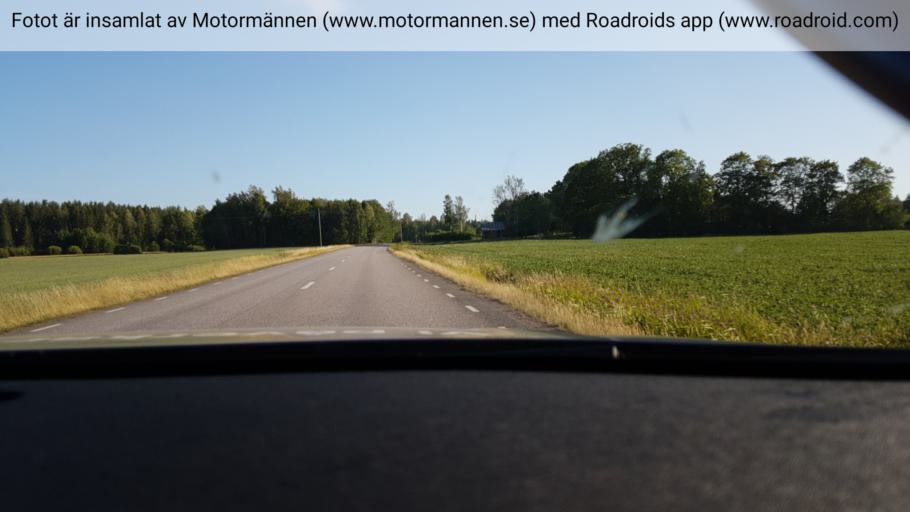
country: SE
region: Vaestra Goetaland
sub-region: Skovde Kommun
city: Stopen
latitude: 58.5298
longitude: 13.9921
